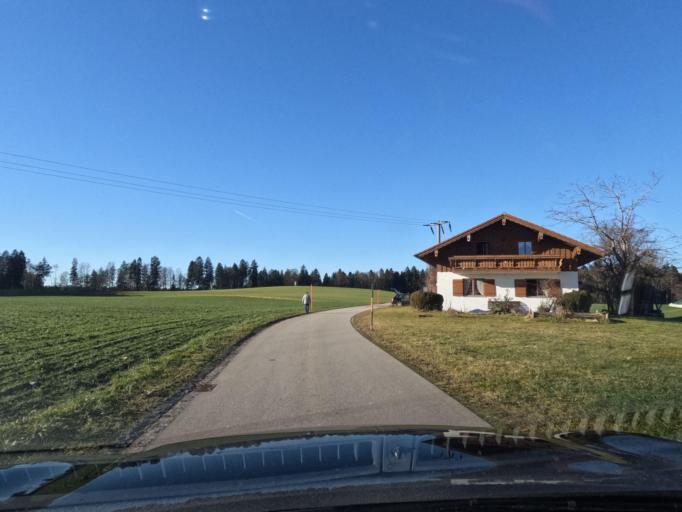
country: DE
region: Bavaria
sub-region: Upper Bavaria
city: Surberg
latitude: 47.8807
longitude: 12.6886
